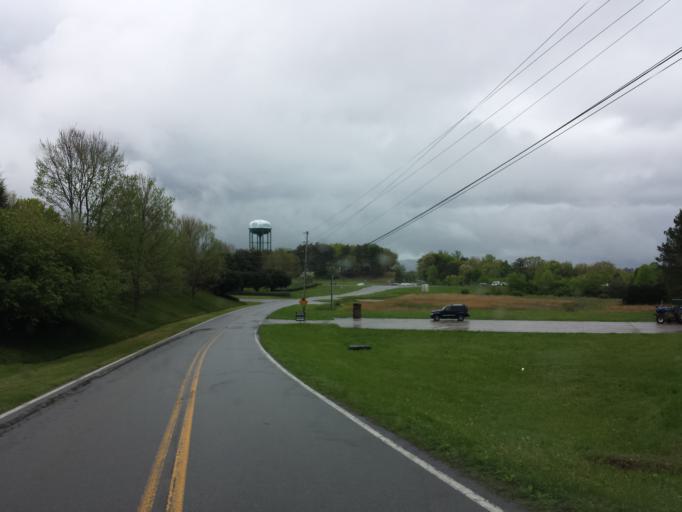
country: US
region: Georgia
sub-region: Pickens County
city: Jasper
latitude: 34.4488
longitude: -84.4526
